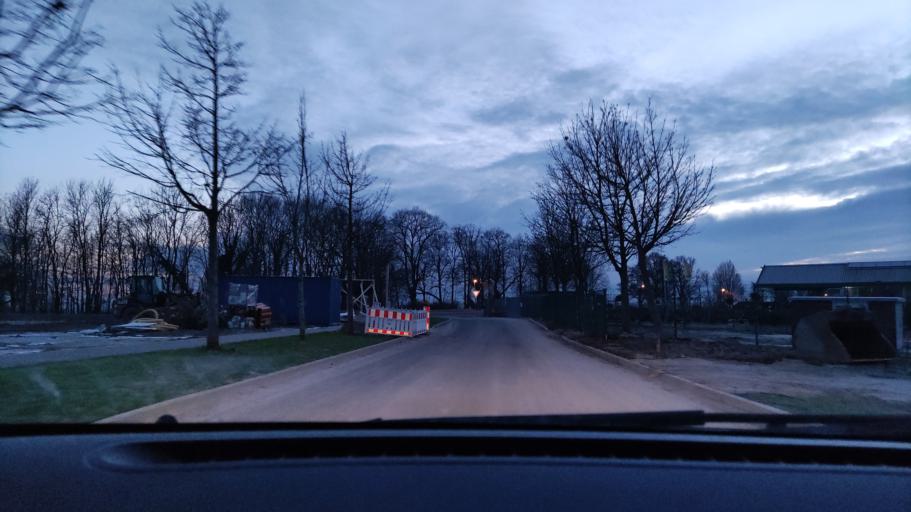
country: DE
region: Mecklenburg-Vorpommern
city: Boizenburg
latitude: 53.3768
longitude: 10.7026
